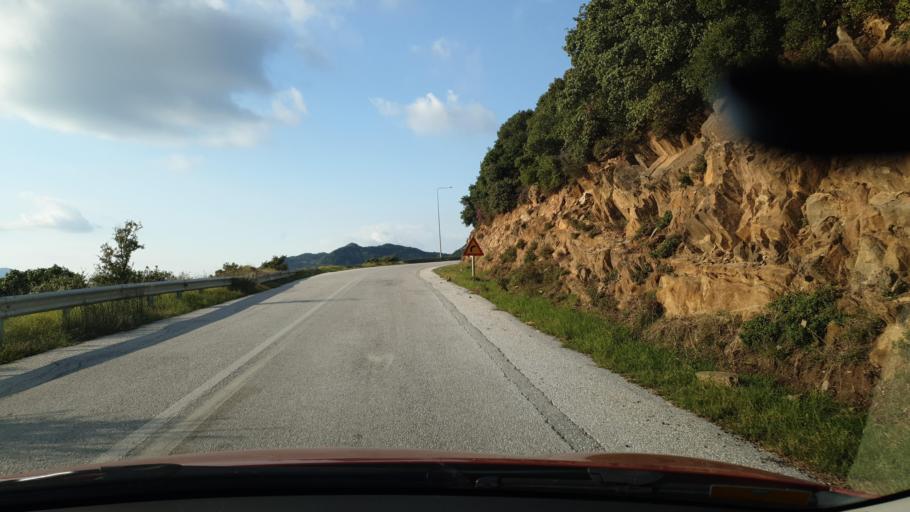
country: GR
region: Central Macedonia
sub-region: Nomos Thessalonikis
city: Peristera
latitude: 40.5200
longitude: 23.2033
